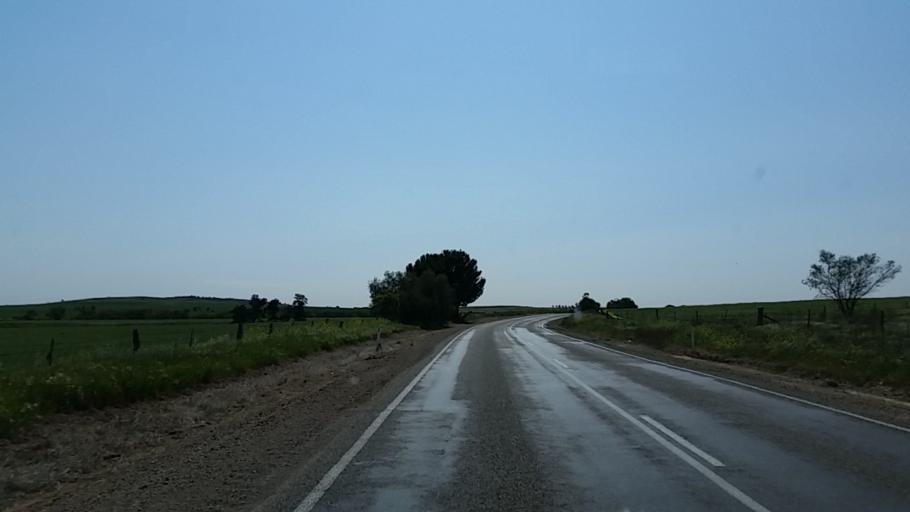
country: AU
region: South Australia
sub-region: Northern Areas
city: Jamestown
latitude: -33.2166
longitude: 138.4160
